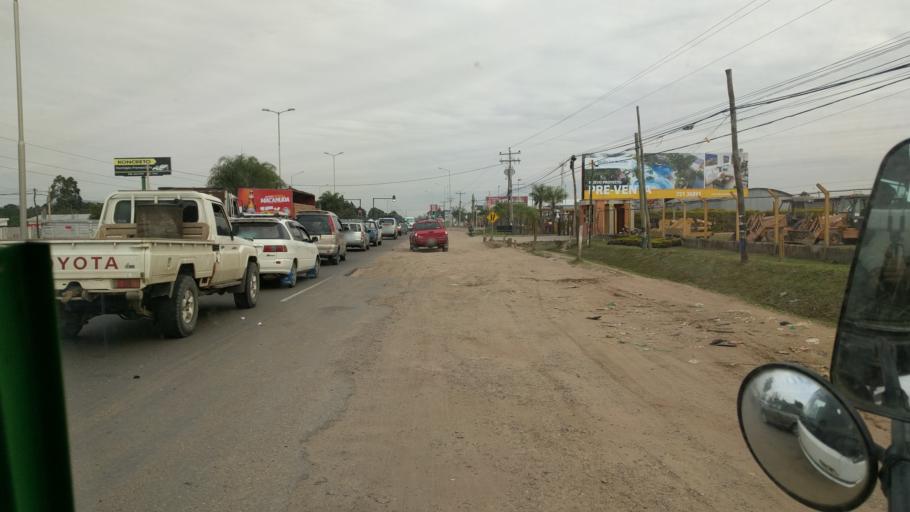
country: BO
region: Santa Cruz
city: Santa Cruz de la Sierra
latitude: -17.6985
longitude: -63.1597
